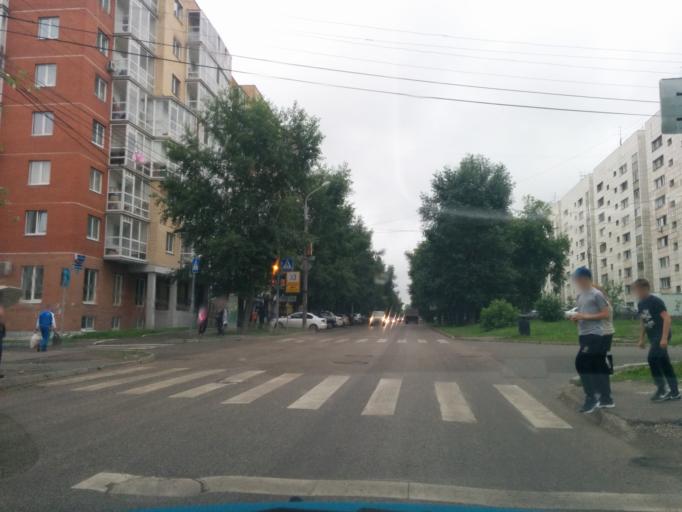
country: RU
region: Perm
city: Perm
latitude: 57.9965
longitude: 56.2261
